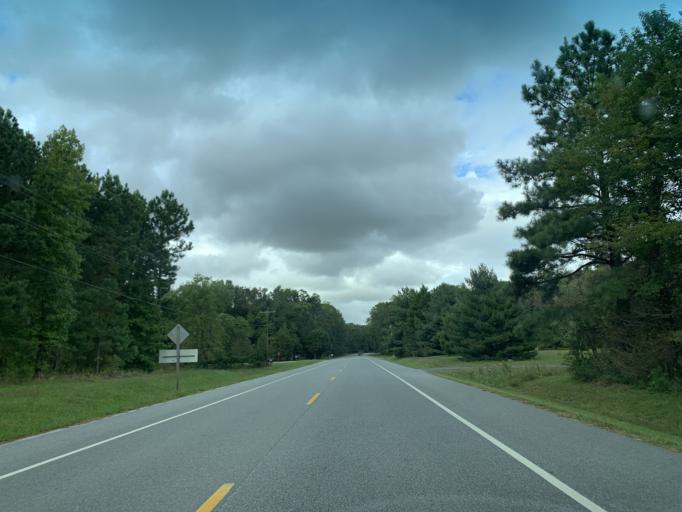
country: US
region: Maryland
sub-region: Caroline County
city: Ridgely
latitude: 39.0216
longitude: -75.8754
